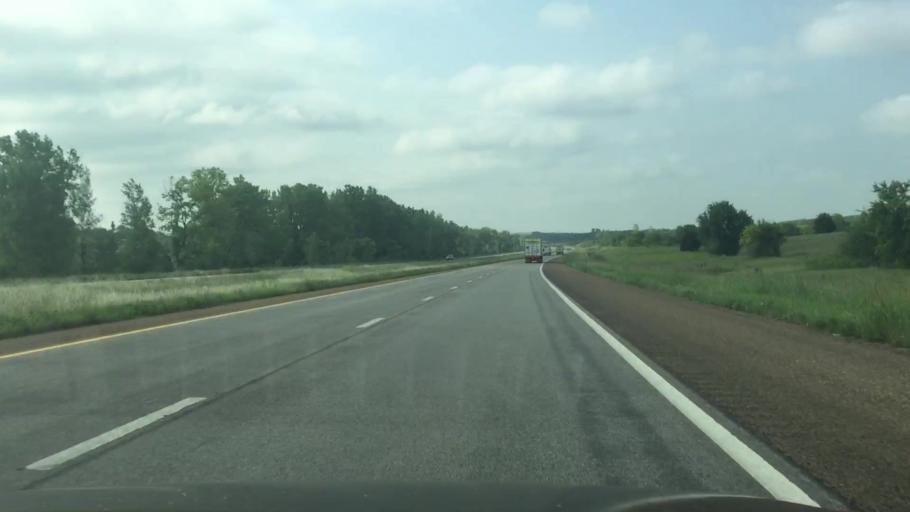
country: US
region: Kansas
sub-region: Johnson County
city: Spring Hill
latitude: 38.7065
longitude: -94.8344
